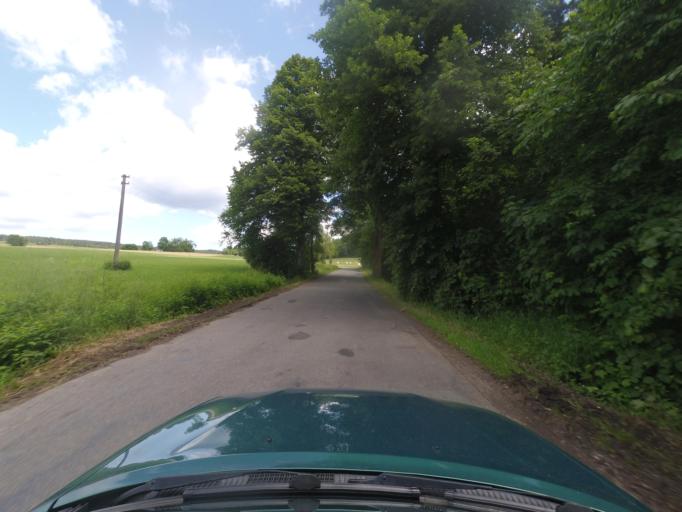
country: CZ
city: Rokytnice v Orlickych Horach
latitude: 50.1276
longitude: 16.4176
